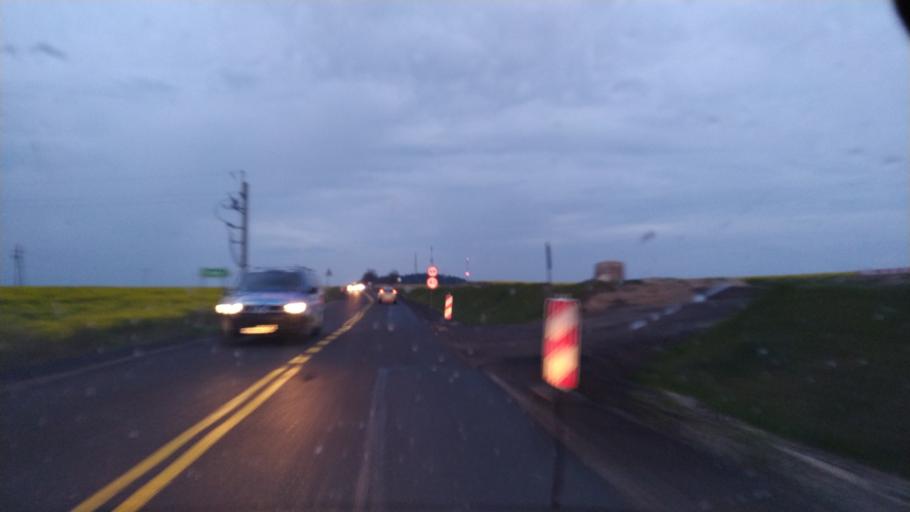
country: PL
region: Greater Poland Voivodeship
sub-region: Powiat pilski
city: Szydlowo
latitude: 53.2443
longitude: 16.6116
